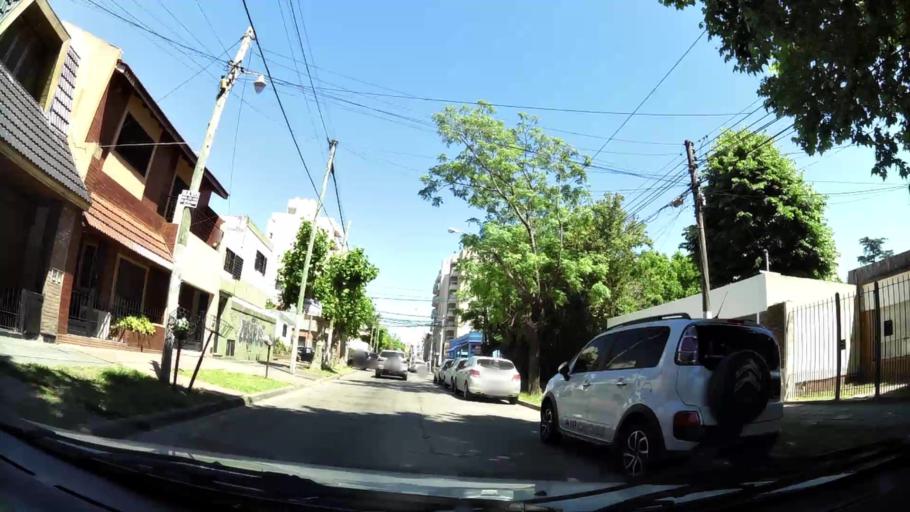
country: AR
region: Buenos Aires
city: Caseros
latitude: -34.6014
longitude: -58.5583
